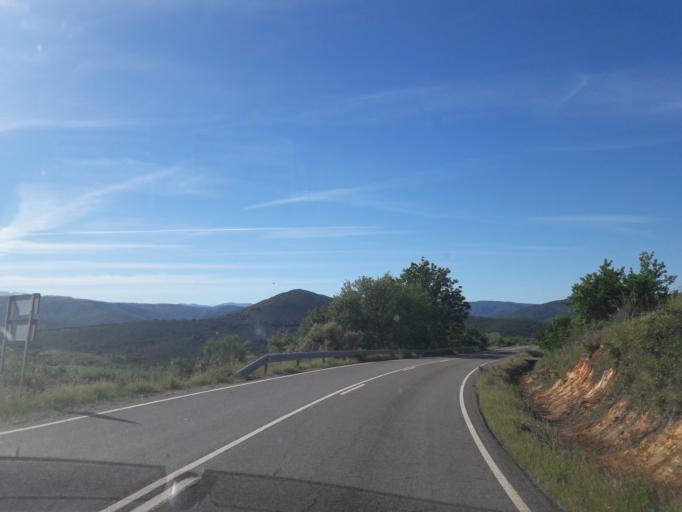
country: ES
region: Castille and Leon
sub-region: Provincia de Salamanca
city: Sotoserrano
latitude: 40.4296
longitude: -6.0333
